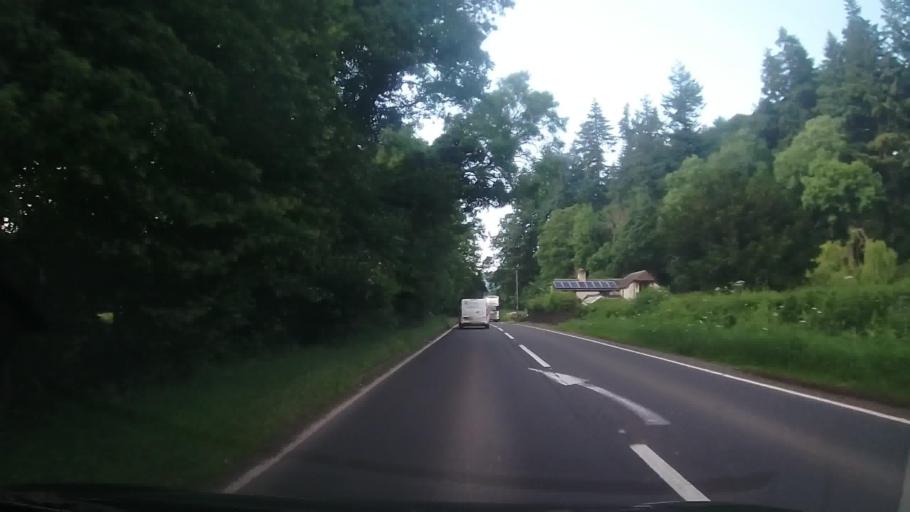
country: GB
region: England
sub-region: Shropshire
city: Church Stretton
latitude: 52.5058
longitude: -2.8244
